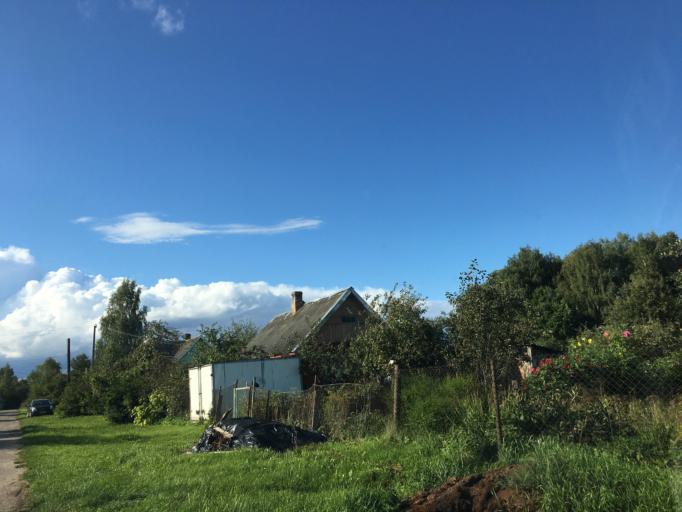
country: RU
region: Pskov
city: Izborsk
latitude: 57.7702
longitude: 27.9741
